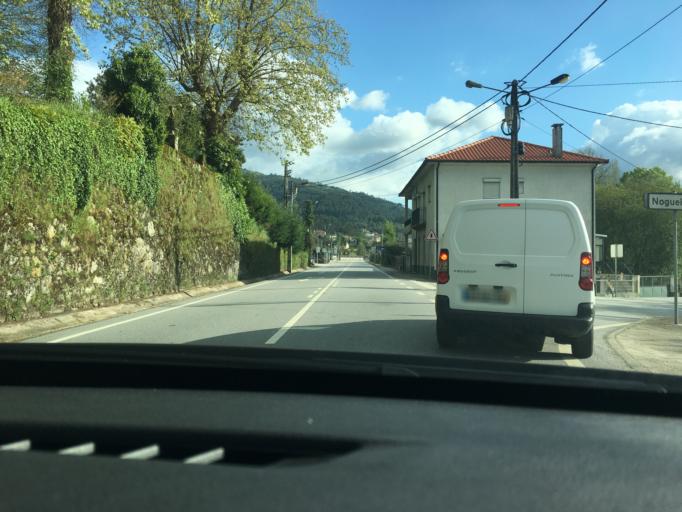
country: PT
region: Viana do Castelo
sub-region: Ponte da Barca
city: Ponte da Barca
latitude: 41.7900
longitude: -8.4140
